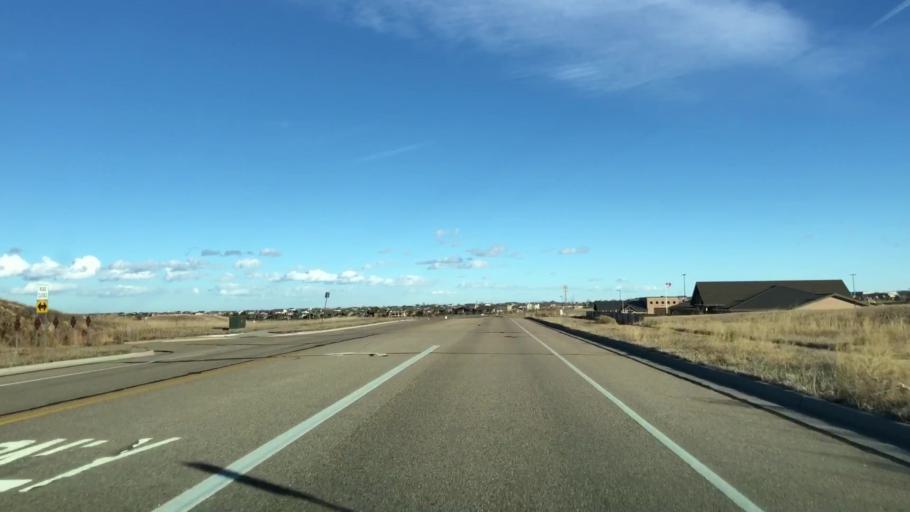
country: US
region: Colorado
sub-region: Weld County
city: Windsor
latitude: 40.4431
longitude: -104.9808
